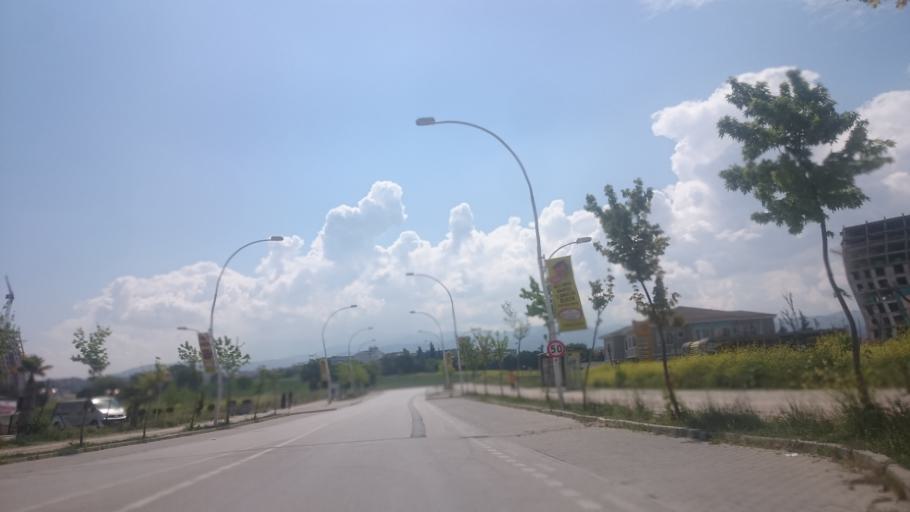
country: TR
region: Bursa
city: Cali
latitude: 40.2162
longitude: 28.9422
